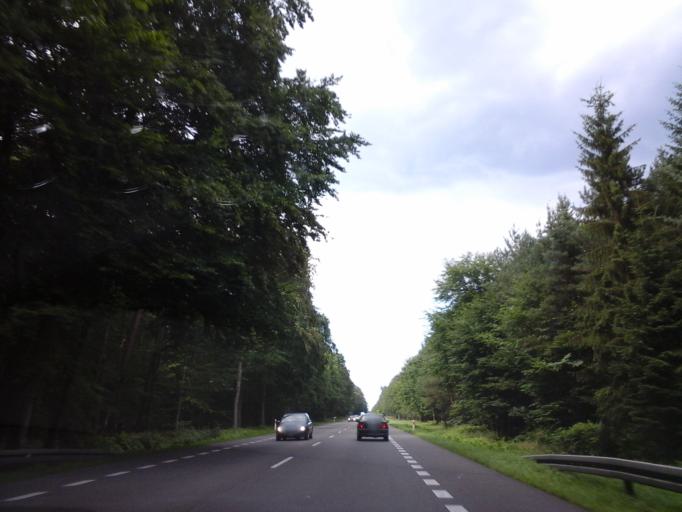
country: PL
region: West Pomeranian Voivodeship
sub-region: Powiat goleniowski
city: Przybiernow
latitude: 53.6900
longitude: 14.7958
